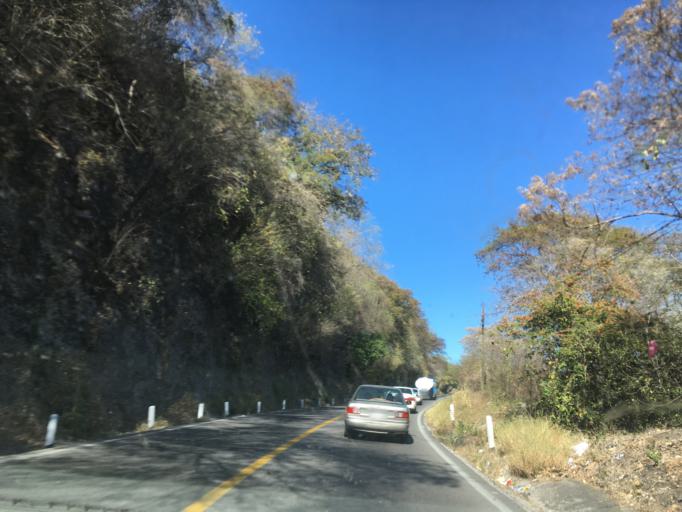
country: MX
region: Michoacan
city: Nueva Italia de Ruiz
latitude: 19.0824
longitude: -102.0625
